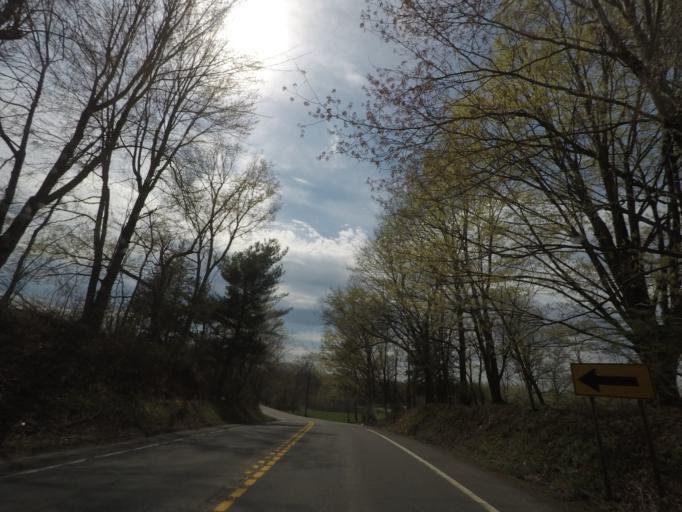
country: US
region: New York
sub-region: Columbia County
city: Philmont
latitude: 42.2959
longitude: -73.6784
